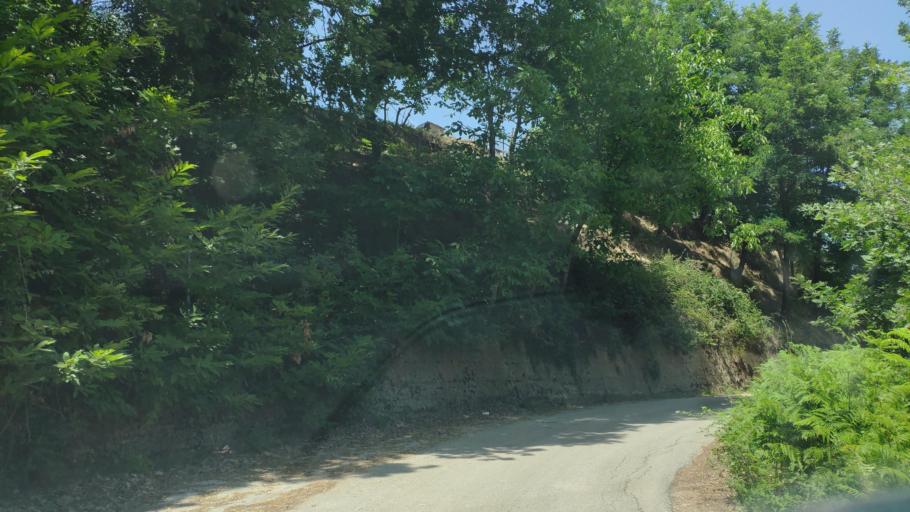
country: GR
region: Epirus
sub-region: Nomos Artas
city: Ano Kalentini
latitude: 39.1994
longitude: 21.3428
